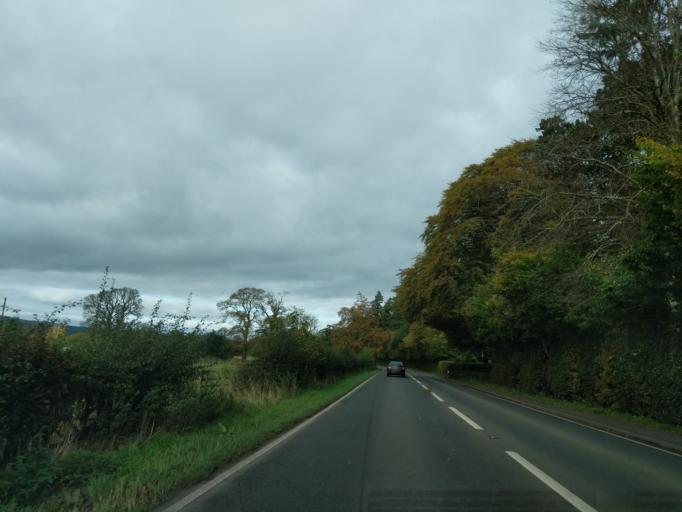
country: GB
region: Scotland
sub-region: Dumfries and Galloway
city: Thornhill
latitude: 55.2562
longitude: -3.7752
